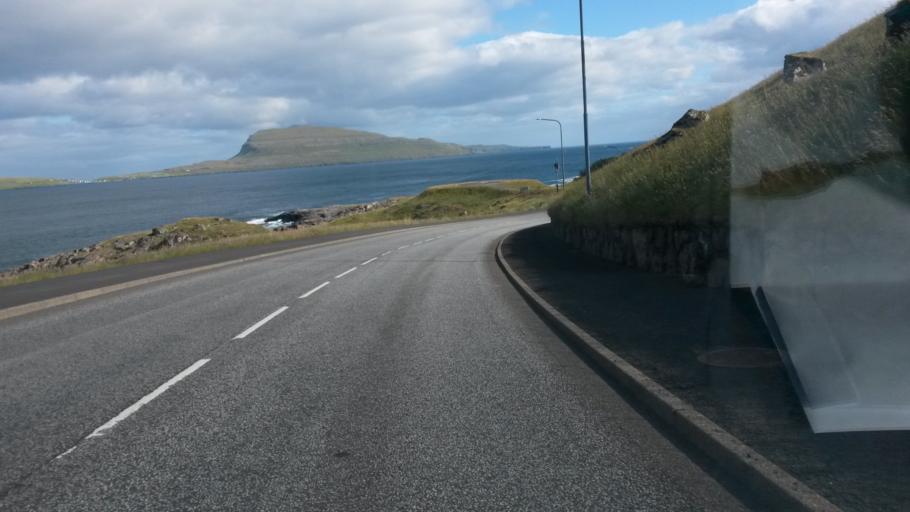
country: FO
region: Streymoy
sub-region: Torshavn
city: Torshavn
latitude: 62.0231
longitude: -6.7600
